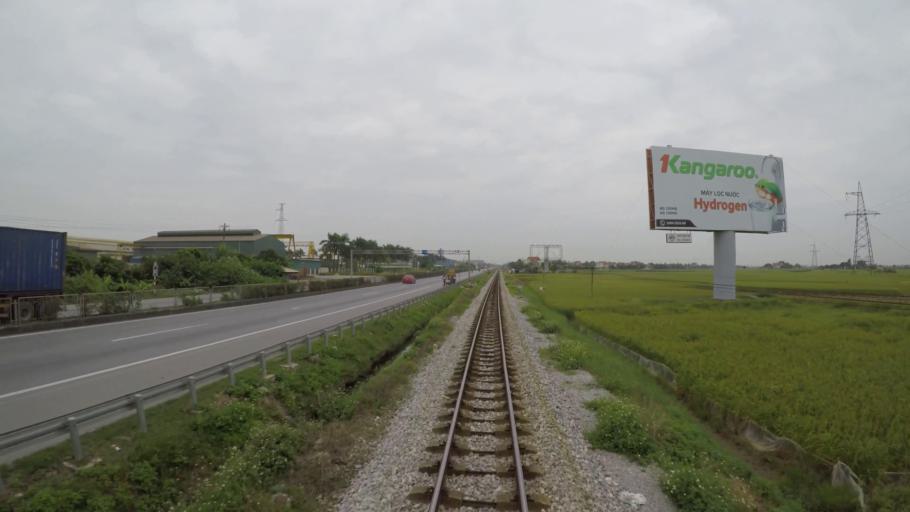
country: VN
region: Hai Duong
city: Phu Thai
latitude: 20.9490
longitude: 106.5348
